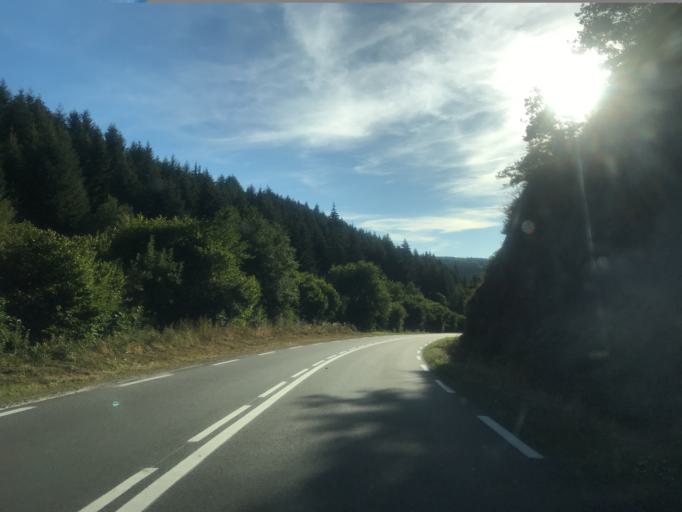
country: FR
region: Limousin
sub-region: Departement de la Creuse
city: Aubusson
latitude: 45.9477
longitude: 2.1826
